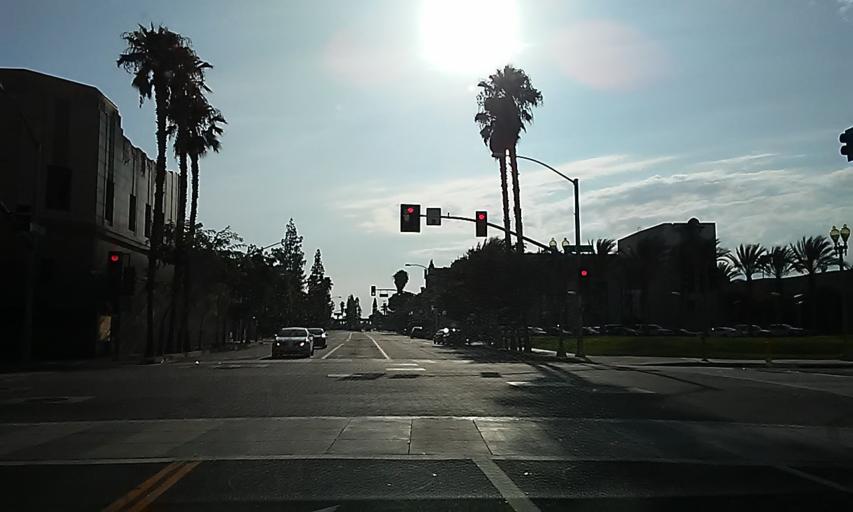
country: US
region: California
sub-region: San Bernardino County
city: San Bernardino
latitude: 34.1065
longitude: -117.2939
